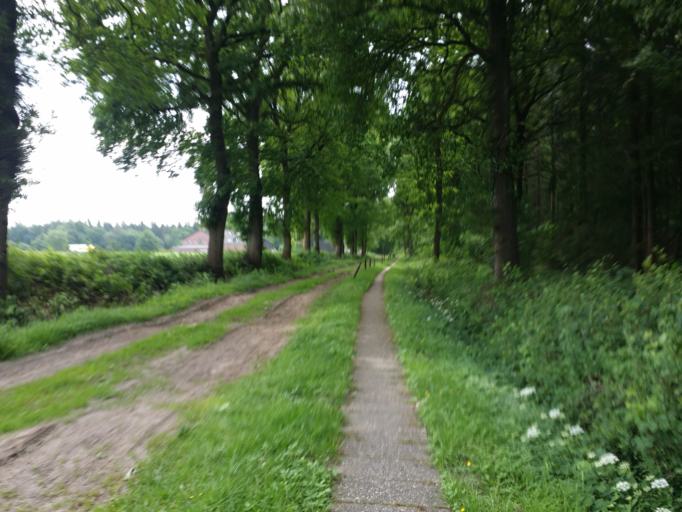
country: DE
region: Lower Saxony
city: Friedeburg
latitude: 53.4998
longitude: 7.8130
